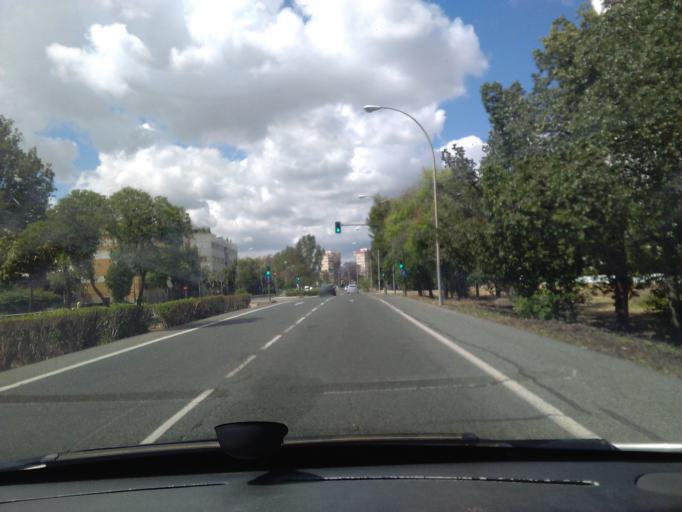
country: ES
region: Andalusia
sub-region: Provincia de Sevilla
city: Sevilla
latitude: 37.3484
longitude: -5.9763
